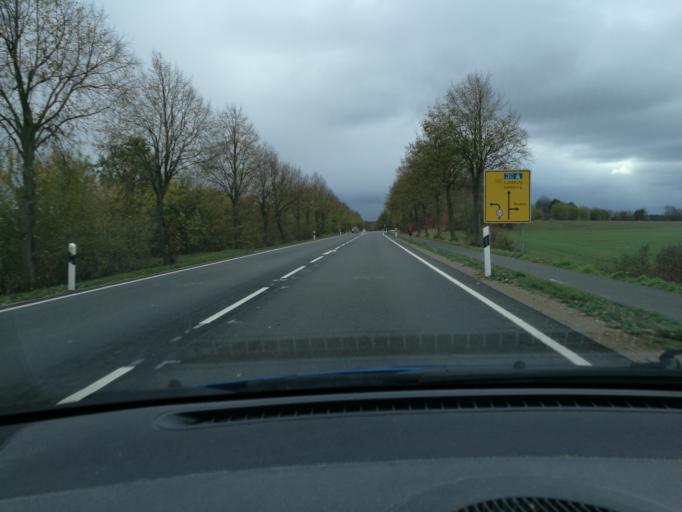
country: DE
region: Schleswig-Holstein
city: Harmsdorf
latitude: 53.6900
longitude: 10.7296
